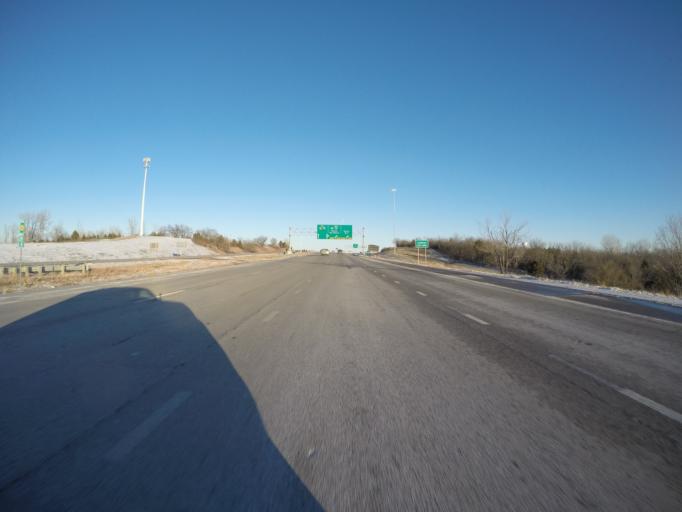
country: US
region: Kansas
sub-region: Johnson County
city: Lenexa
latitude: 38.9413
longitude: -94.7897
